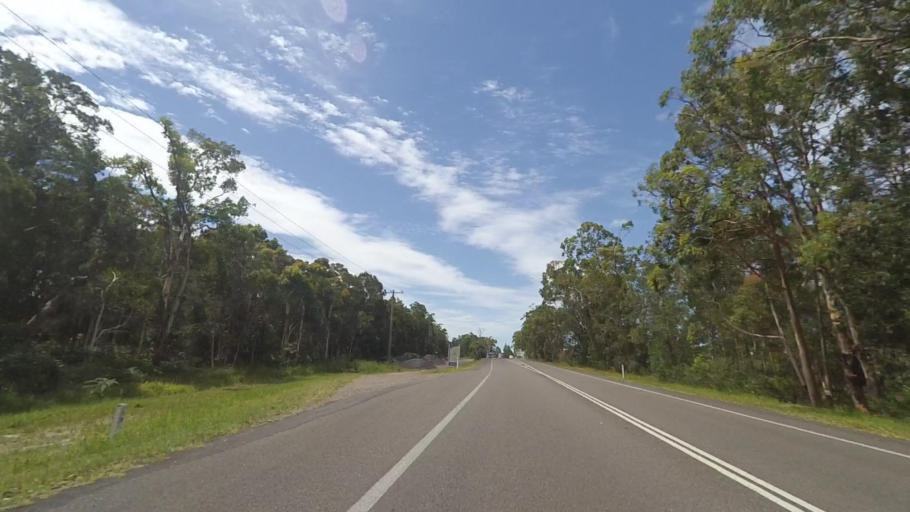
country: AU
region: New South Wales
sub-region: Port Stephens Shire
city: Anna Bay
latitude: -32.7557
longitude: 152.0682
